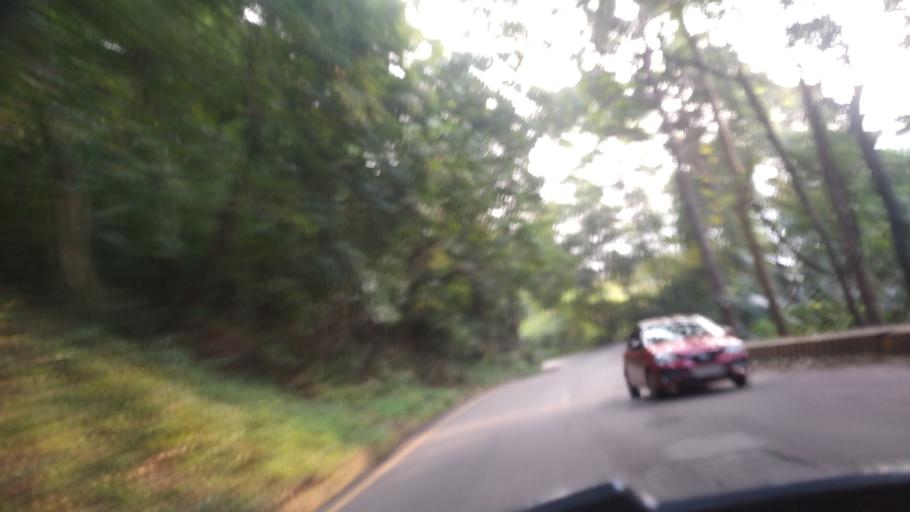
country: IN
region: Kerala
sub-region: Wayanad
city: Kalpetta
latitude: 11.5006
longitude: 76.0254
